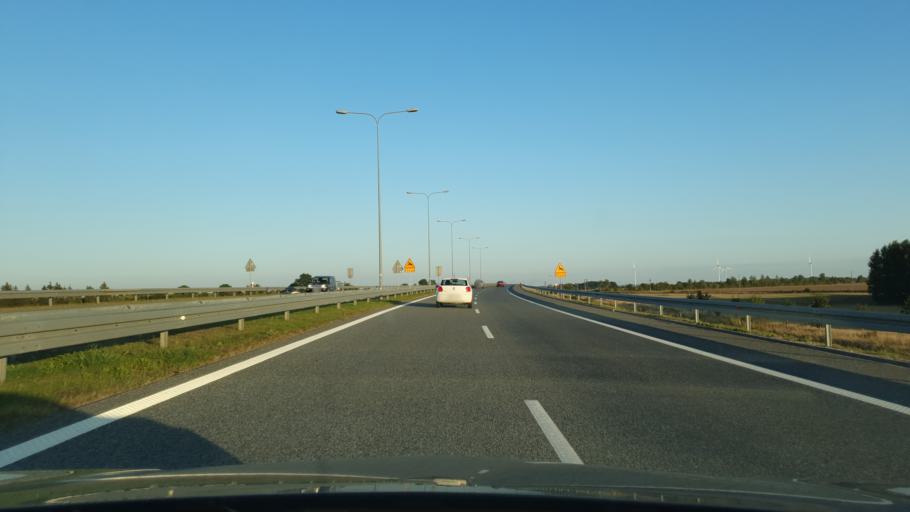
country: PL
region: Pomeranian Voivodeship
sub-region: Powiat slupski
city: Kobylnica
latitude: 54.4406
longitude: 16.9464
